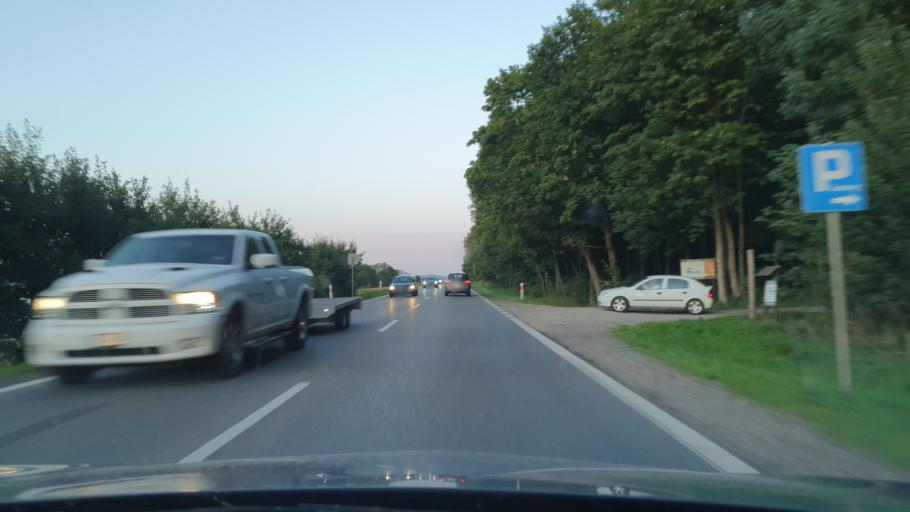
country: PL
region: Pomeranian Voivodeship
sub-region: Powiat wejherowski
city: Leczyce
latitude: 54.5607
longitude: 17.8255
